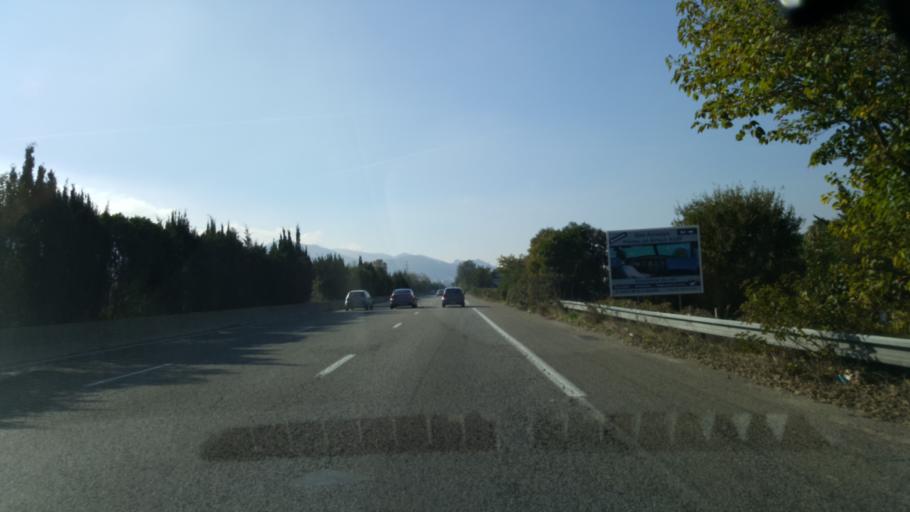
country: FR
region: Provence-Alpes-Cote d'Azur
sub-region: Departement des Bouches-du-Rhone
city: La Penne-sur-Huveaune
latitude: 43.2874
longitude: 5.5418
